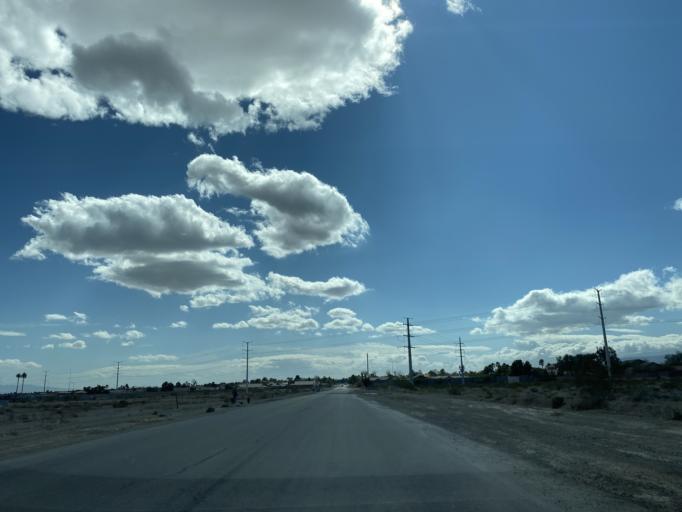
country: US
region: Nevada
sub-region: Clark County
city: Summerlin South
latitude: 36.2435
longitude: -115.2884
